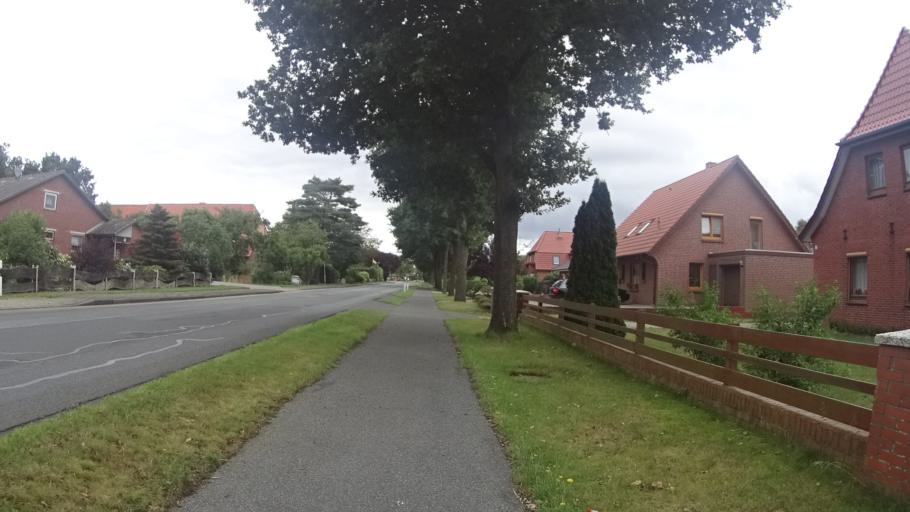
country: DE
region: Lower Saxony
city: Schiffdorf
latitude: 53.5493
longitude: 8.6943
